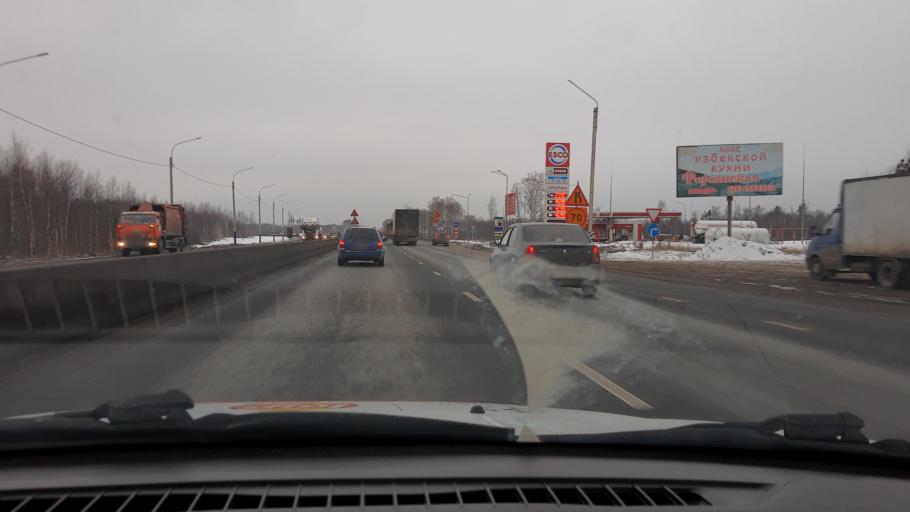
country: RU
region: Nizjnij Novgorod
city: Babino
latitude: 56.3041
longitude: 43.6108
